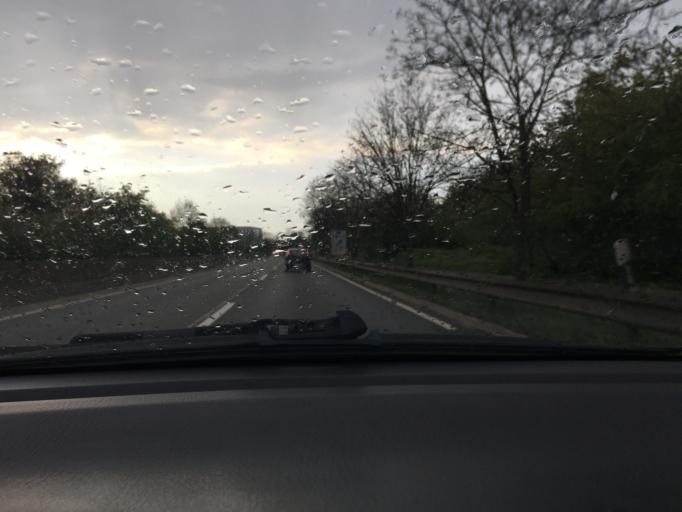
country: DE
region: Rheinland-Pfalz
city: Sankt Sebastian
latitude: 50.4178
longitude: 7.5719
